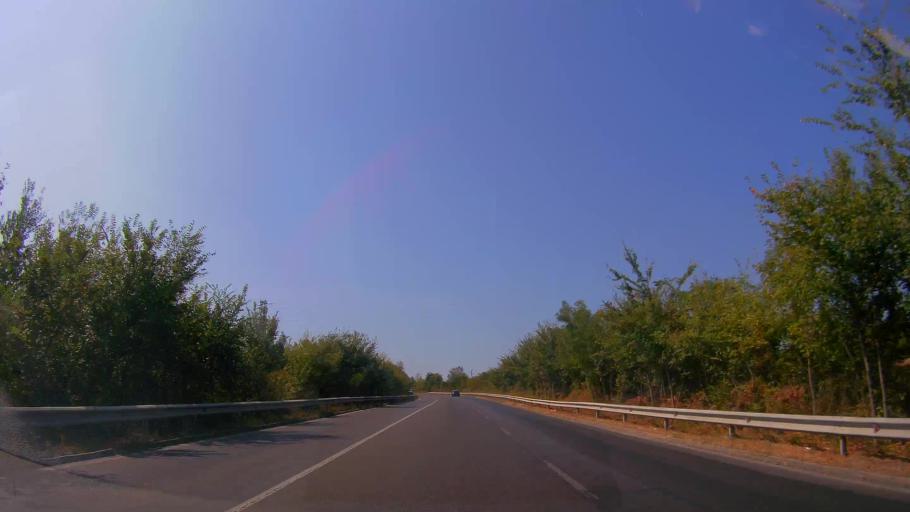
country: BG
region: Ruse
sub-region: Obshtina Vetovo
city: Senovo
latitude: 43.5612
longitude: 26.3804
